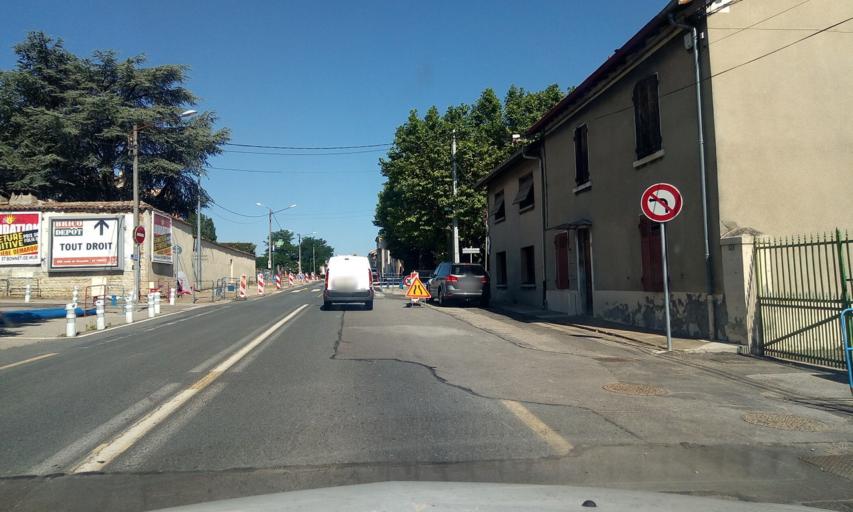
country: FR
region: Rhone-Alpes
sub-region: Departement du Rhone
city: Saint-Laurent-de-Mure
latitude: 45.6867
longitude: 5.0503
